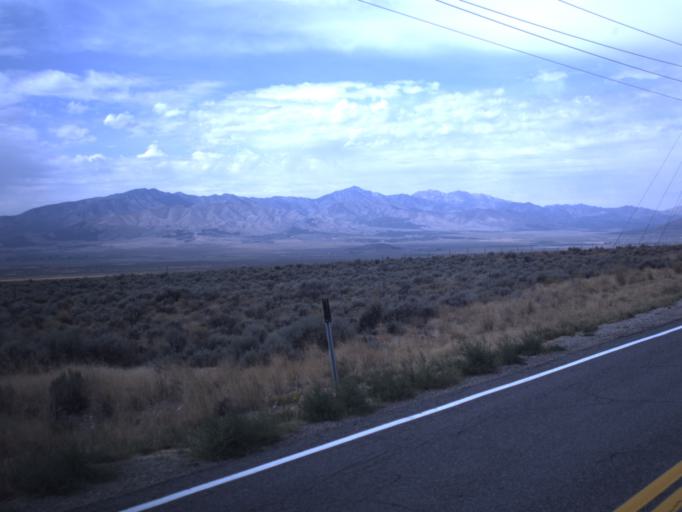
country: US
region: Utah
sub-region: Tooele County
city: Tooele
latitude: 40.3502
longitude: -112.3098
